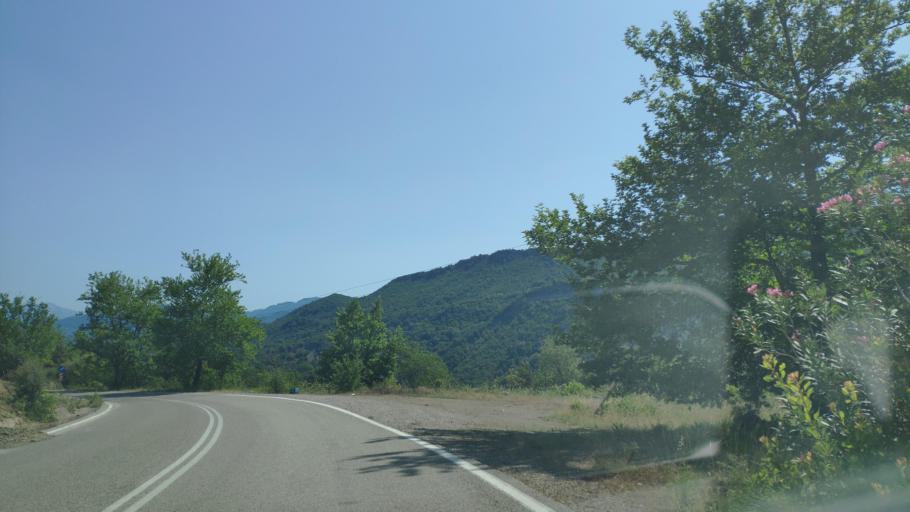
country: GR
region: West Greece
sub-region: Nomos Aitolias kai Akarnanias
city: Lepenou
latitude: 38.7997
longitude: 21.3323
